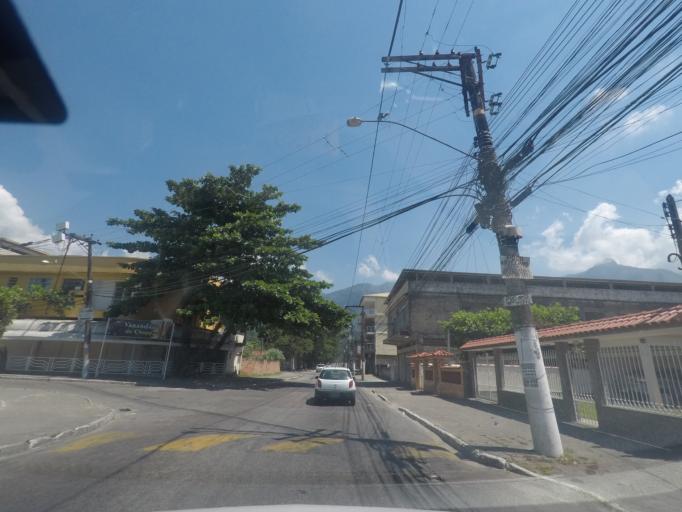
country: BR
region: Rio de Janeiro
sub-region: Petropolis
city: Petropolis
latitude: -22.5859
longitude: -43.1861
